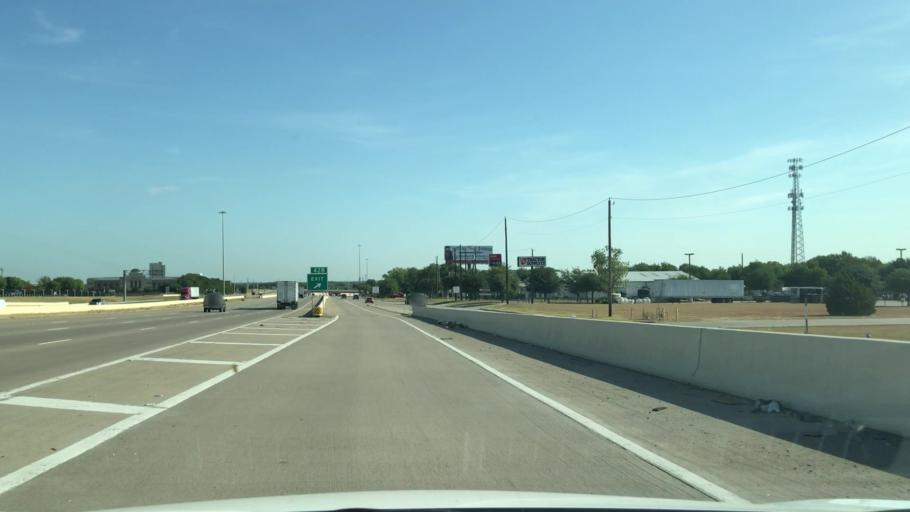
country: US
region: Texas
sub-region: Collin County
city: McKinney
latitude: 33.2318
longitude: -96.6320
